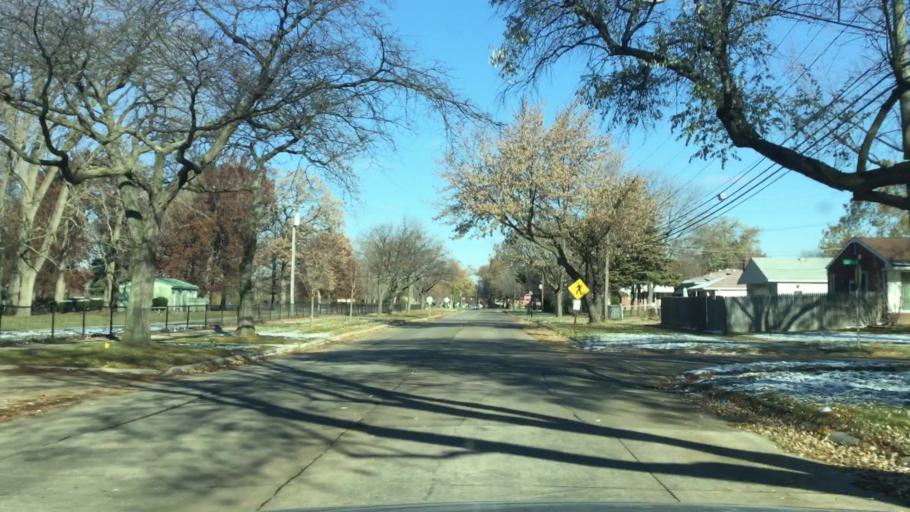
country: US
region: Michigan
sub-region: Oakland County
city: Hazel Park
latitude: 42.4567
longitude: -83.0740
